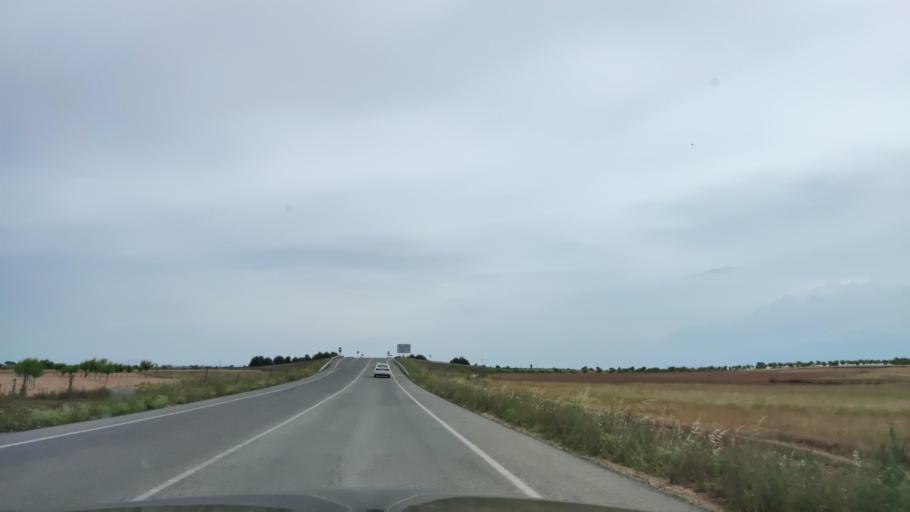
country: ES
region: Castille-La Mancha
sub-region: Provincia de Albacete
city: La Roda
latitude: 39.2236
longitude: -2.1895
